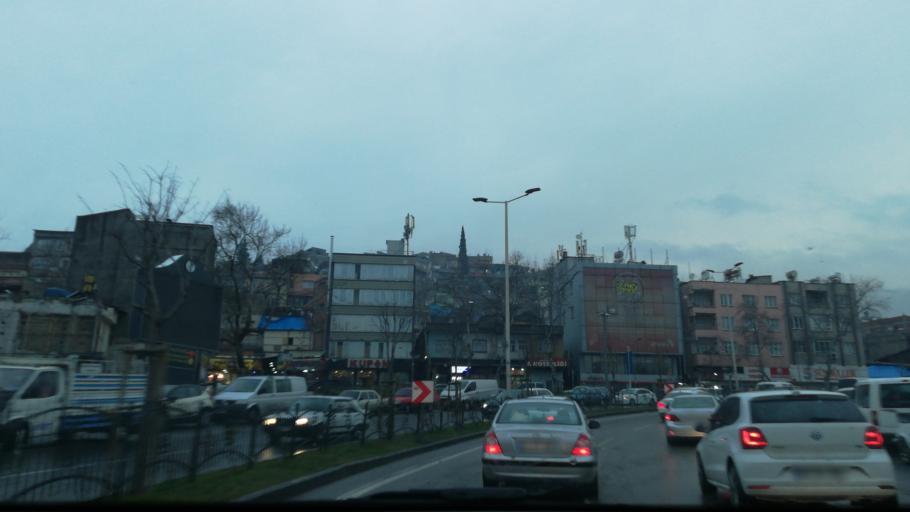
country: TR
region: Kahramanmaras
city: Kahramanmaras
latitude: 37.5822
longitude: 36.9265
